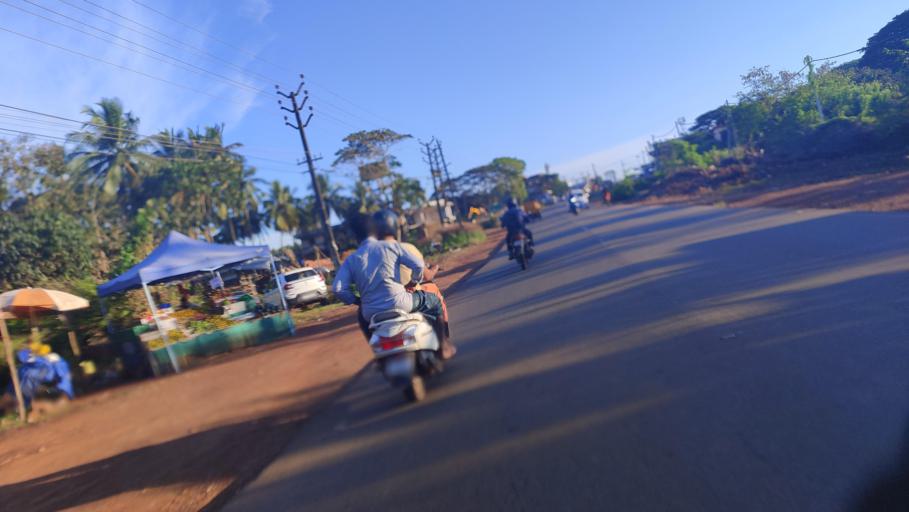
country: IN
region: Kerala
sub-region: Kasaragod District
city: Kasaragod
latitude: 12.4823
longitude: 75.0574
